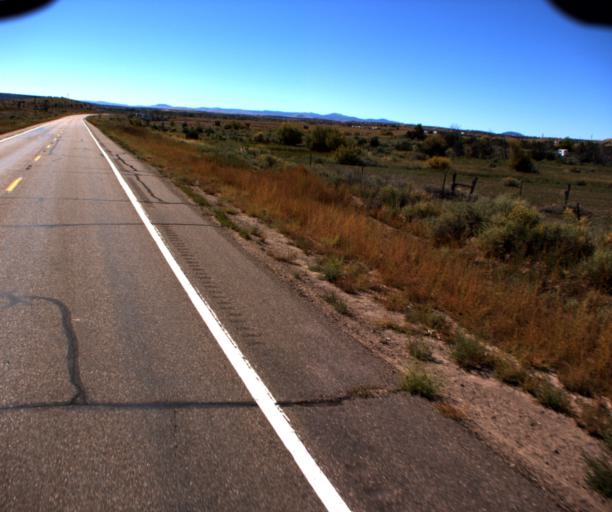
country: US
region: Arizona
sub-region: Apache County
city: Saint Johns
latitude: 34.4309
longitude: -109.4107
